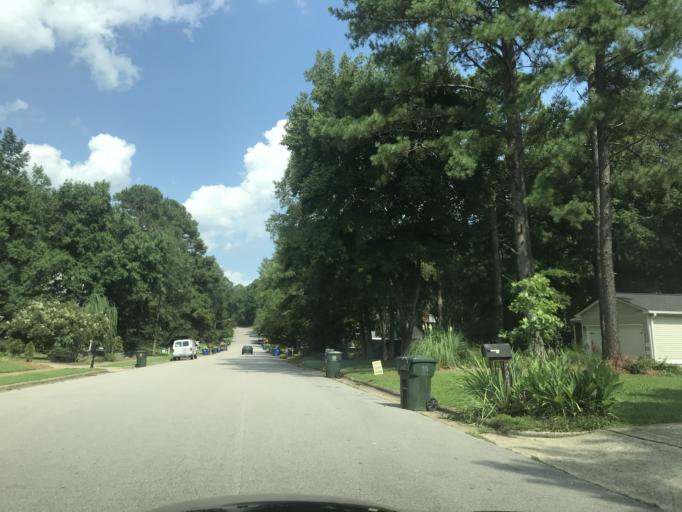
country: US
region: North Carolina
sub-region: Wake County
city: West Raleigh
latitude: 35.8761
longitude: -78.6607
